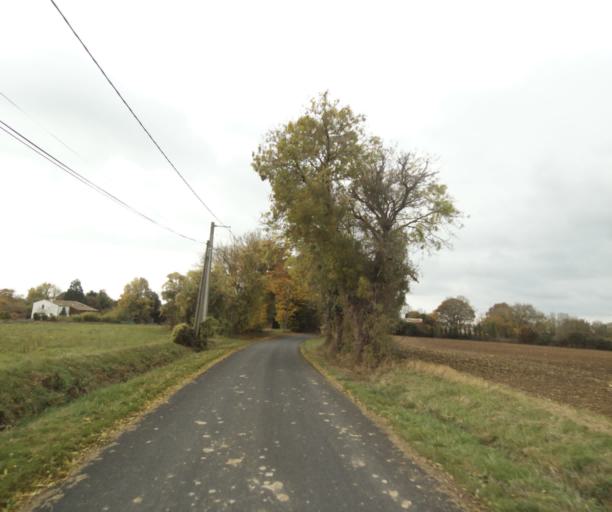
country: FR
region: Poitou-Charentes
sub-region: Departement de la Charente-Maritime
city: Saint-Georges-des-Coteaux
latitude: 45.7800
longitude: -0.6916
